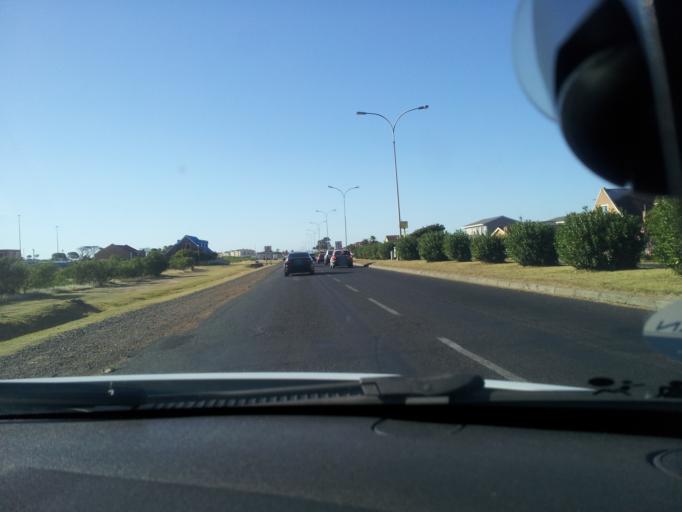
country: ZA
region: Western Cape
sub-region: Overberg District Municipality
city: Grabouw
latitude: -34.1408
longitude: 18.8510
